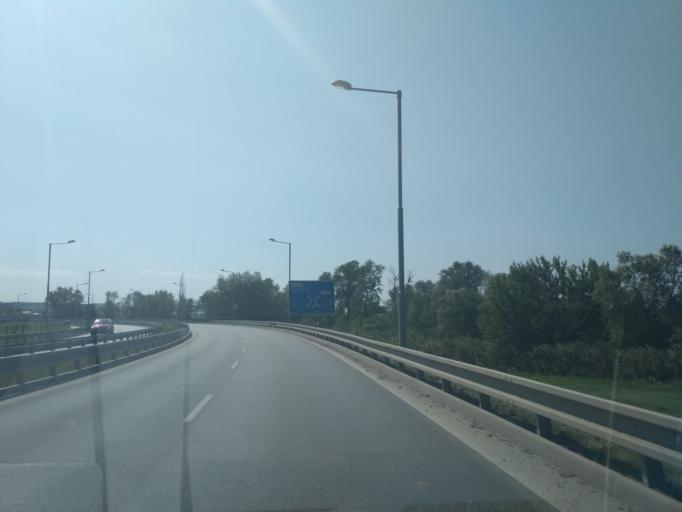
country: SK
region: Presovsky
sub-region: Okres Presov
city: Presov
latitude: 48.9708
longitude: 21.2467
